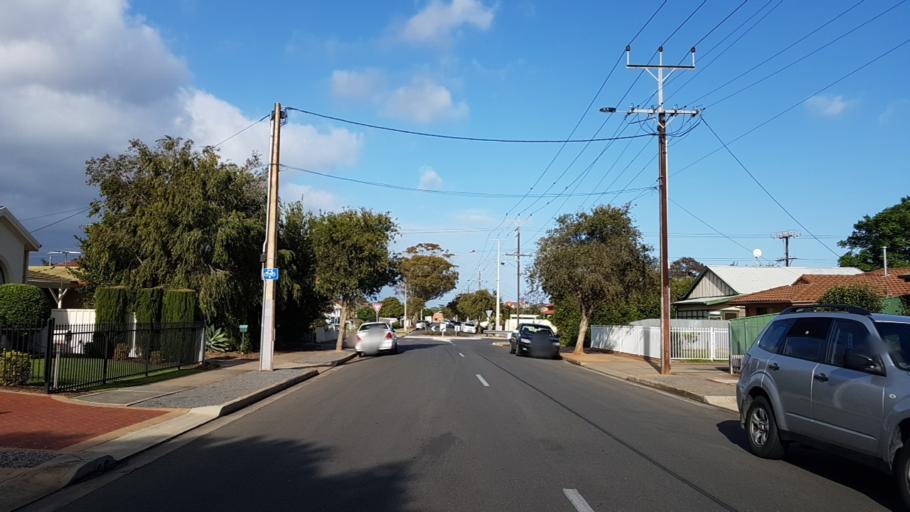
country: AU
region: South Australia
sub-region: Marion
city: South Plympton
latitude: -34.9867
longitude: 138.5618
